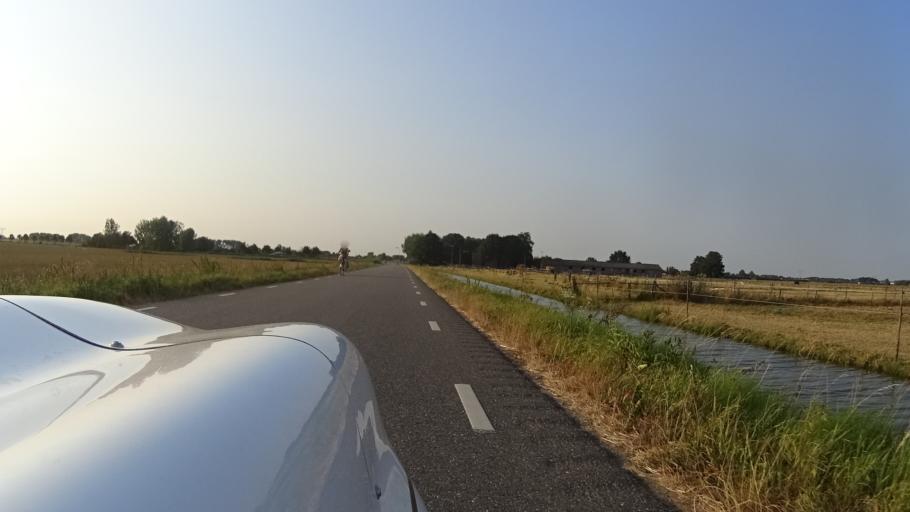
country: NL
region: Gelderland
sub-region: Gemeente Buren
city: Lienden
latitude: 51.8612
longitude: 5.5158
